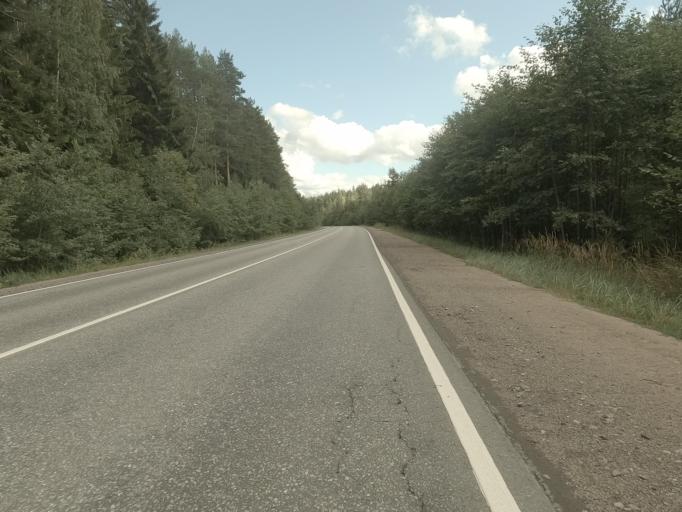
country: RU
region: Leningrad
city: Shcheglovo
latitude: 60.0118
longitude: 30.8550
